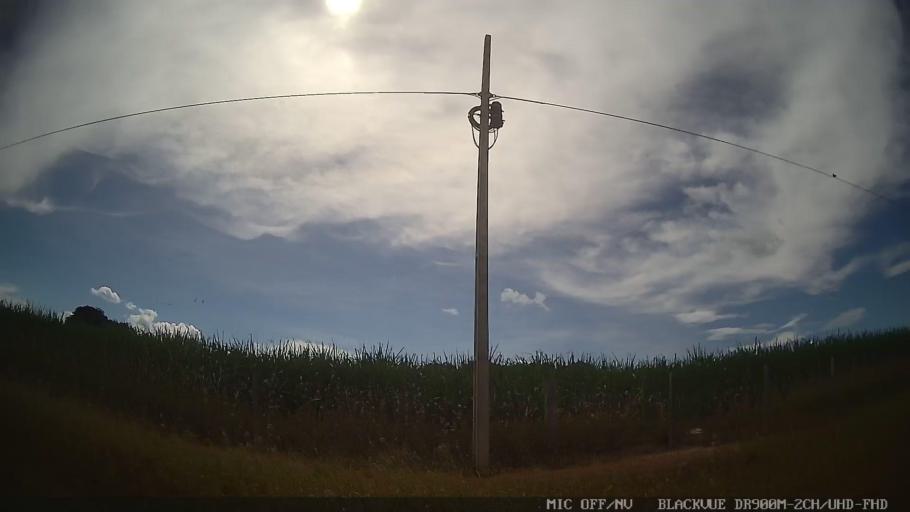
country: BR
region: Sao Paulo
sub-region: Conchas
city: Conchas
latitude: -22.9788
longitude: -47.9888
